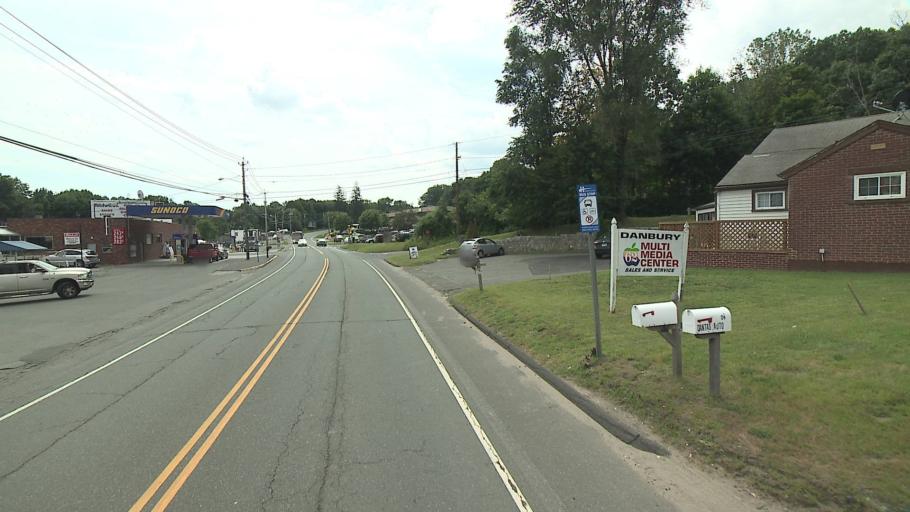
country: US
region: Connecticut
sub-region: Fairfield County
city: Danbury
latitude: 41.4071
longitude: -73.4297
